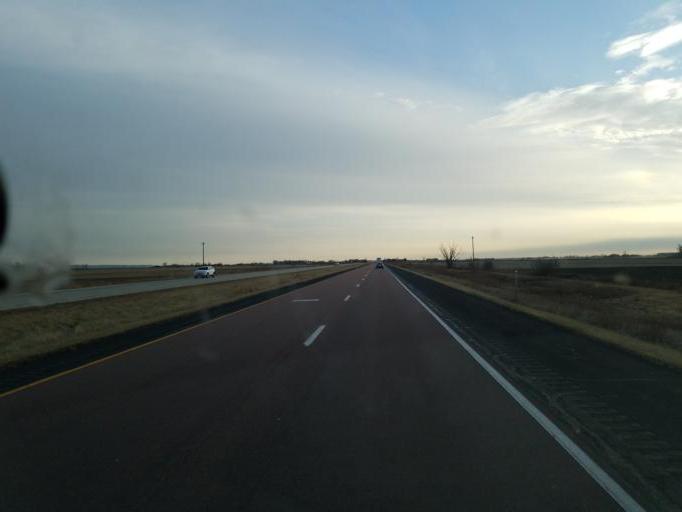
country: US
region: Iowa
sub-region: Monona County
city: Onawa
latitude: 41.9469
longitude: -96.1037
